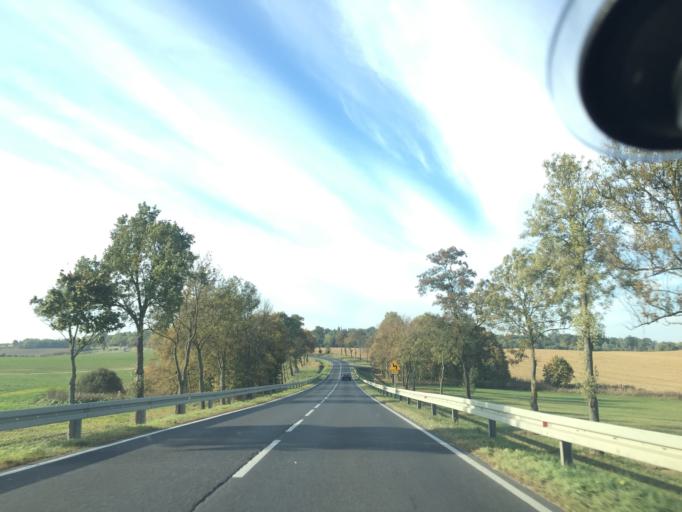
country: PL
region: Warmian-Masurian Voivodeship
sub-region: Powiat lidzbarski
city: Lidzbark Warminski
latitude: 54.1107
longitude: 20.5635
